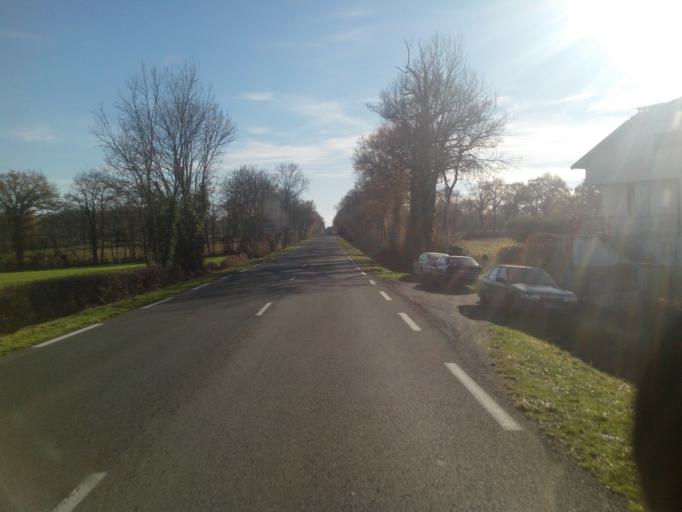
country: FR
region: Limousin
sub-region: Departement de la Haute-Vienne
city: Bussiere-Poitevine
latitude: 46.2281
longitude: 0.8999
